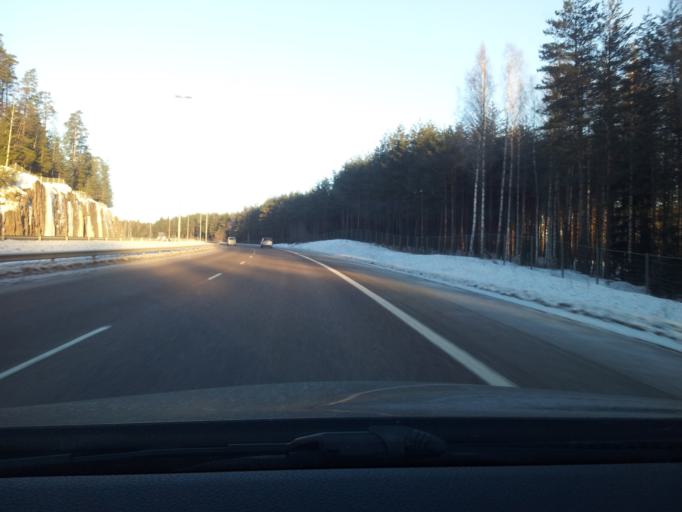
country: FI
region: Uusimaa
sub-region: Helsinki
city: Kirkkonummi
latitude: 60.2643
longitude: 24.4859
